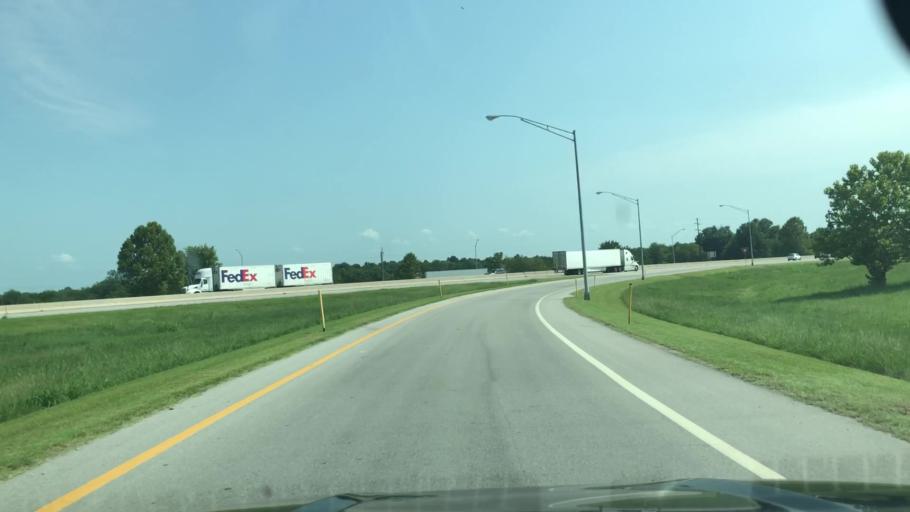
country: US
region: Oklahoma
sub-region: Ottawa County
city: Miami
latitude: 36.8647
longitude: -94.8513
